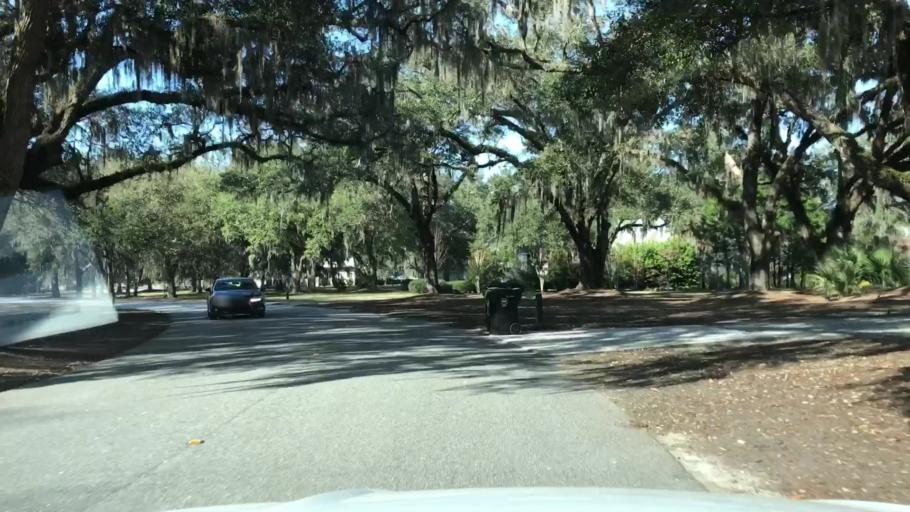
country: US
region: South Carolina
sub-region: Beaufort County
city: Bluffton
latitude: 32.3375
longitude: -80.9101
